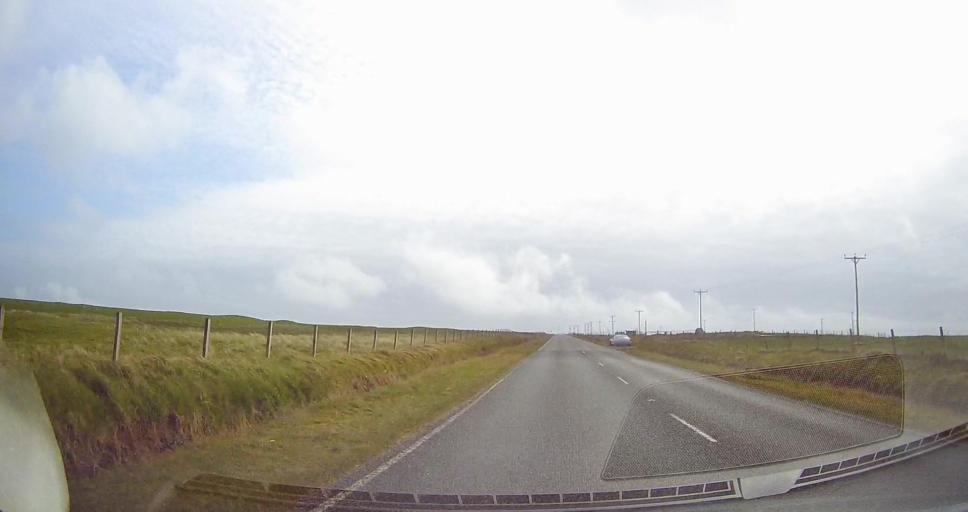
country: GB
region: Scotland
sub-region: Shetland Islands
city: Sandwick
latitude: 59.9028
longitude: -1.3030
